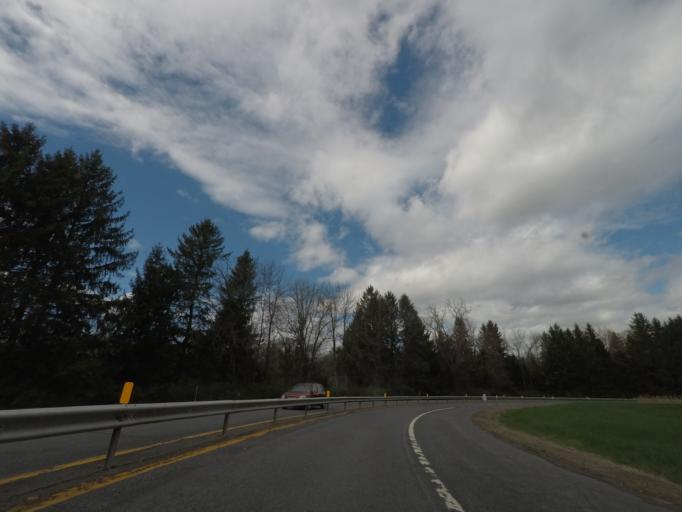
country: US
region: New York
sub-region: Rensselaer County
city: Castleton-on-Hudson
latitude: 42.5331
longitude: -73.7867
